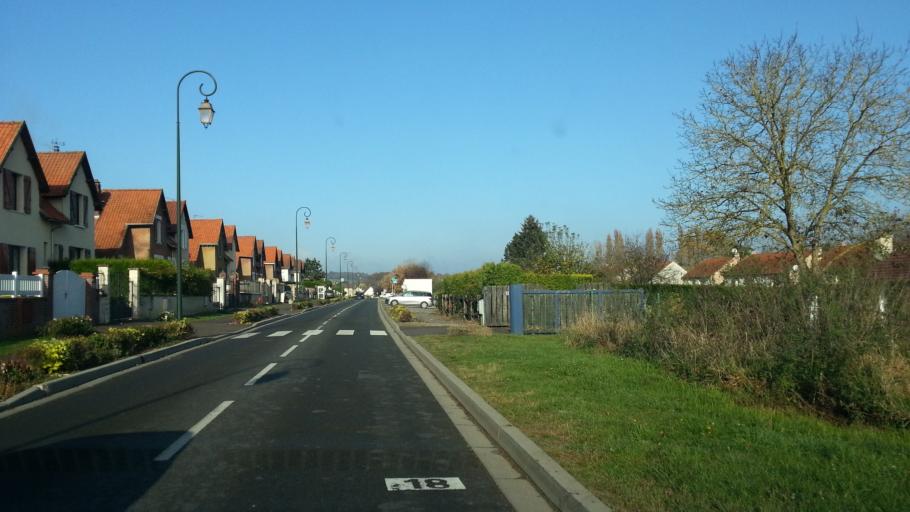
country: FR
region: Picardie
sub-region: Departement de l'Oise
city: Balagny-sur-Therain
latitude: 49.2884
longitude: 2.3431
